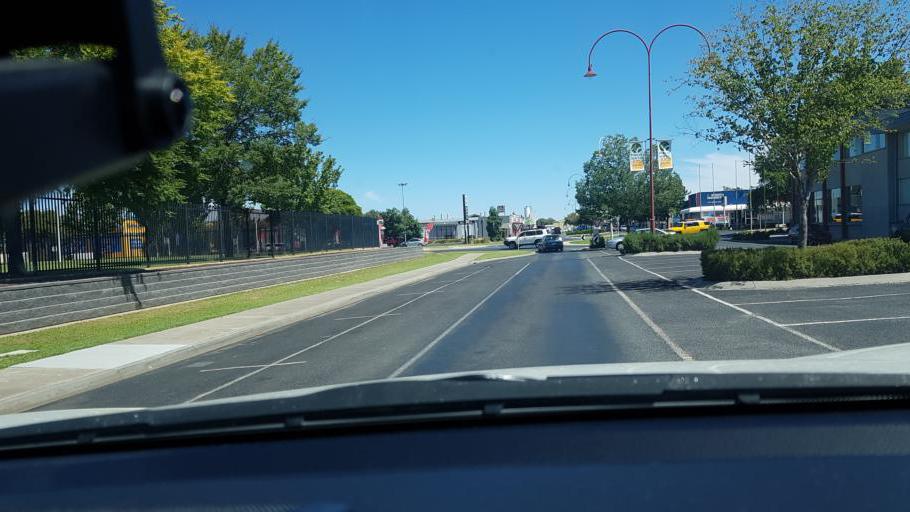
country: AU
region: Victoria
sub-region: Horsham
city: Horsham
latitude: -36.7179
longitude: 142.2009
